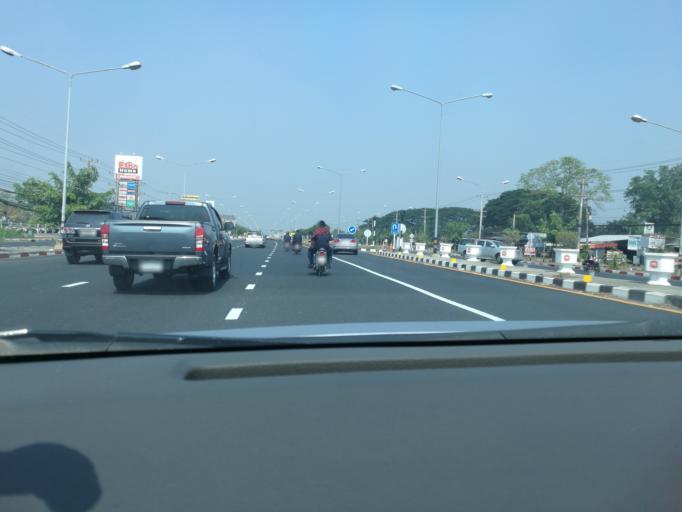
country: TH
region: Sara Buri
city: Saraburi
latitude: 14.5493
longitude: 100.9078
